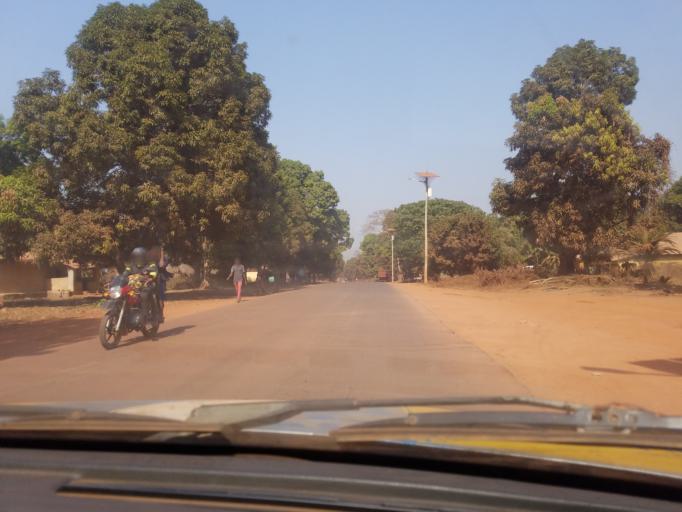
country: GN
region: Boke
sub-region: Boke Prefecture
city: Sangueya
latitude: 10.8065
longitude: -14.3878
